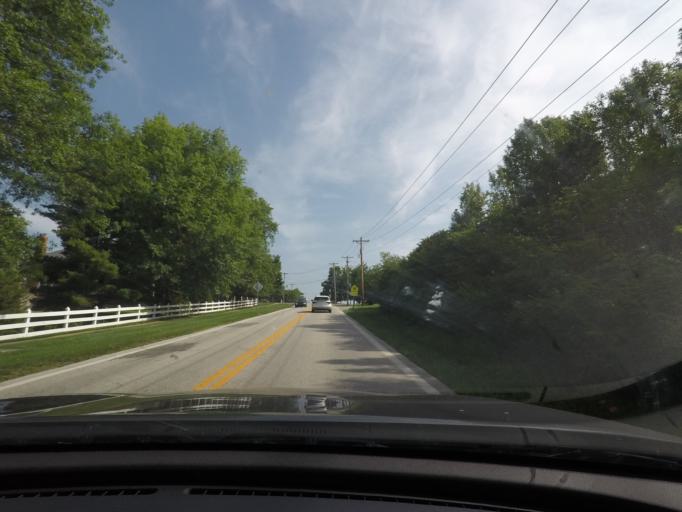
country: US
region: Missouri
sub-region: Saint Louis County
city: Town and Country
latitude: 38.6349
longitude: -90.4811
